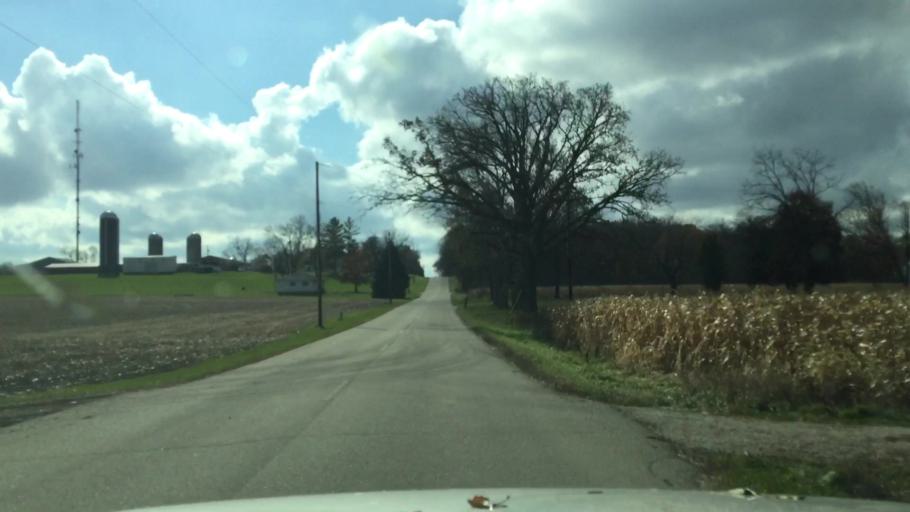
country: US
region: Wisconsin
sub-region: Racine County
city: Eagle Lake
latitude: 42.7525
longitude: -88.1554
